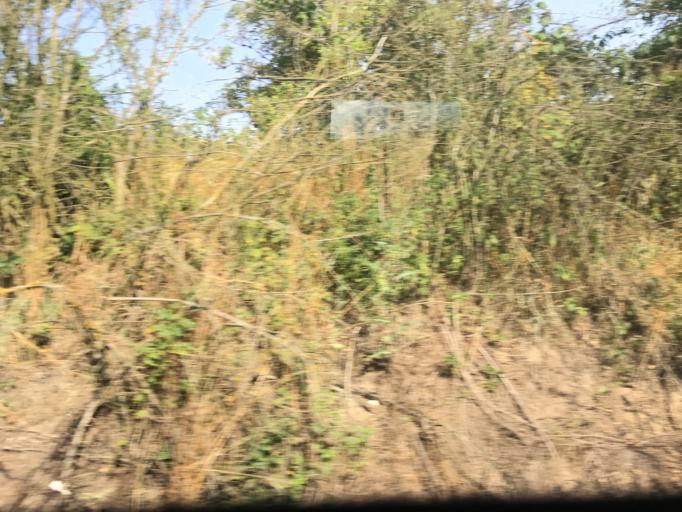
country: CZ
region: Central Bohemia
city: Votice
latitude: 49.6087
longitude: 14.5820
